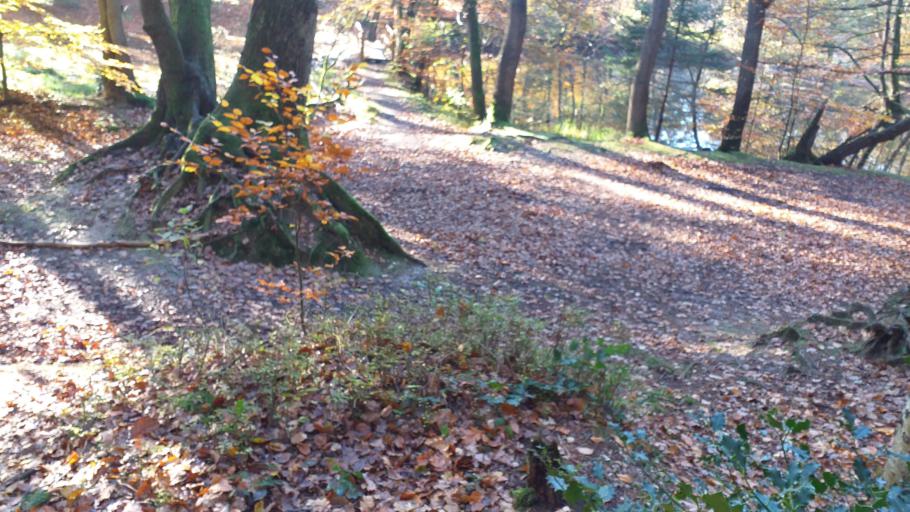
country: BE
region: Wallonia
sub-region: Province de Liege
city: La Calamine
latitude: 50.7323
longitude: 6.0471
